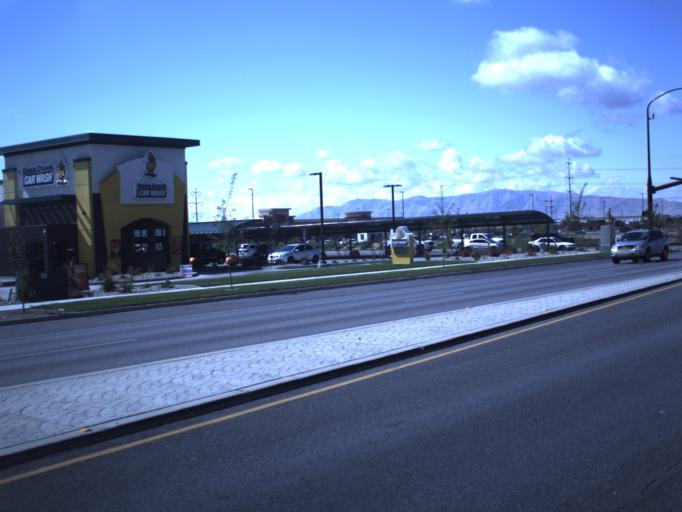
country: US
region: Utah
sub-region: Utah County
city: Springville
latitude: 40.1612
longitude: -111.6269
